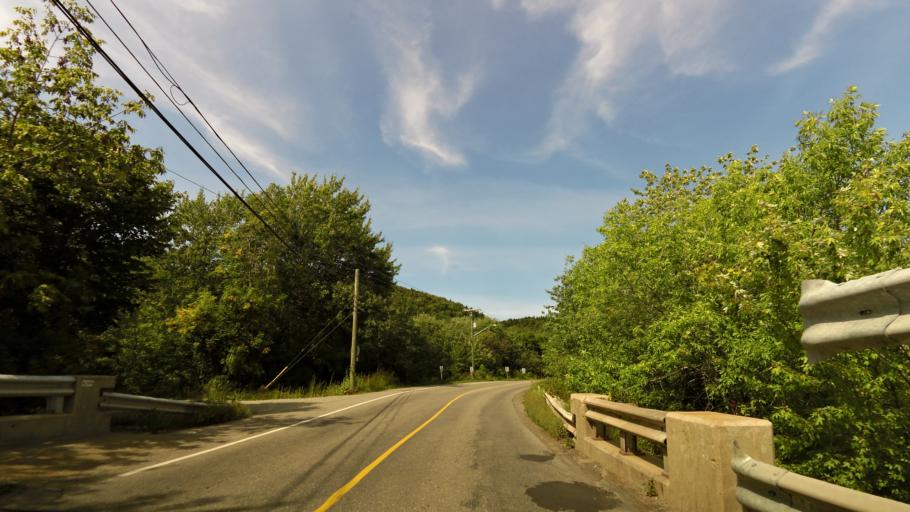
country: CA
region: New Brunswick
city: Hampton
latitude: 45.5437
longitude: -65.8368
